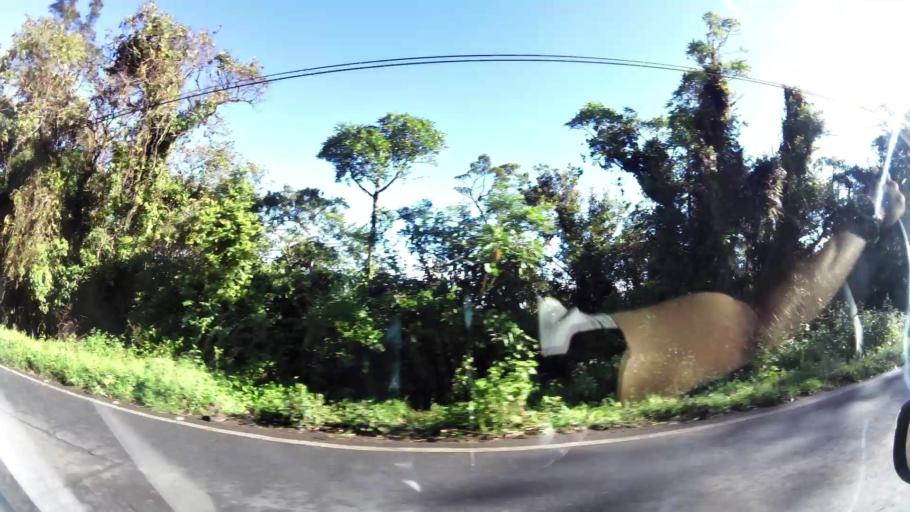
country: CR
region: San Jose
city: San Marcos
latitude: 9.6957
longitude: -83.9275
